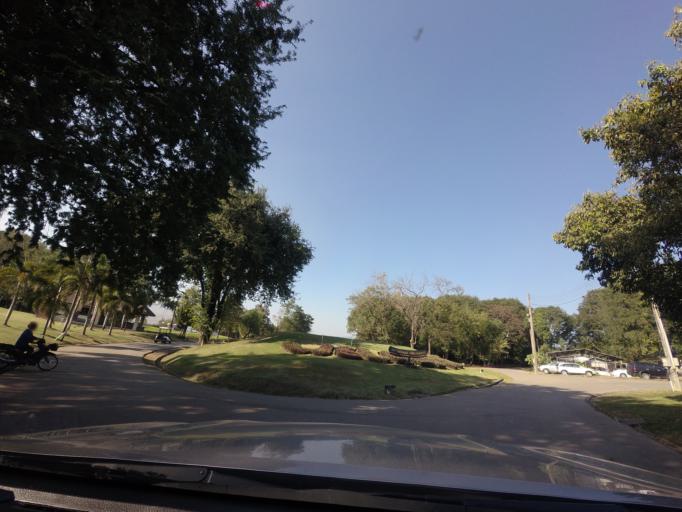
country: TH
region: Lampang
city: Mae Mo
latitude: 18.3215
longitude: 99.7438
